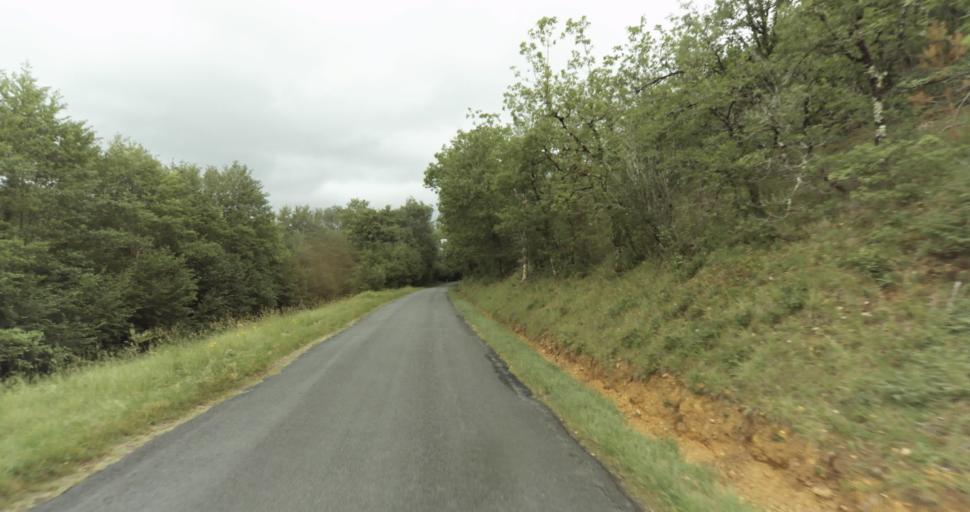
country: FR
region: Aquitaine
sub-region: Departement de la Dordogne
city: Beaumont-du-Perigord
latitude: 44.7525
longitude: 0.8301
